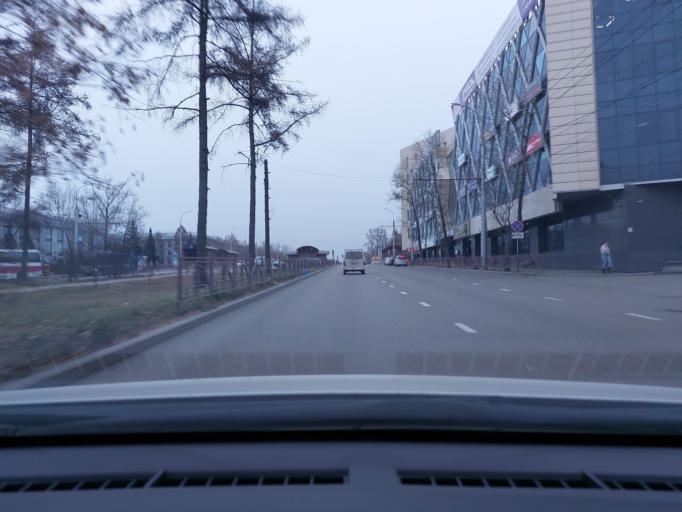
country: RU
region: Irkutsk
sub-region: Irkutskiy Rayon
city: Irkutsk
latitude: 52.2636
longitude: 104.2593
